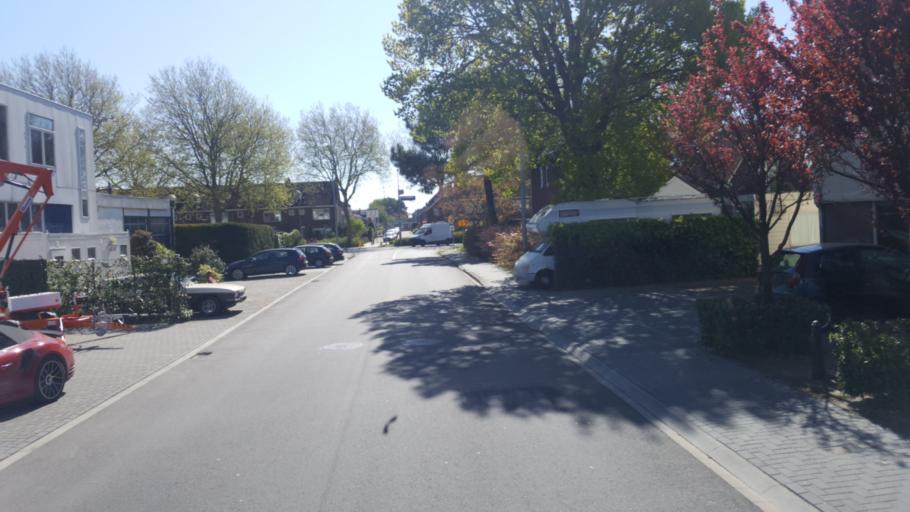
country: NL
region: North Holland
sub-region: Gemeente Haarlemmermeer
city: Hoofddorp
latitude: 52.3813
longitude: 4.7397
